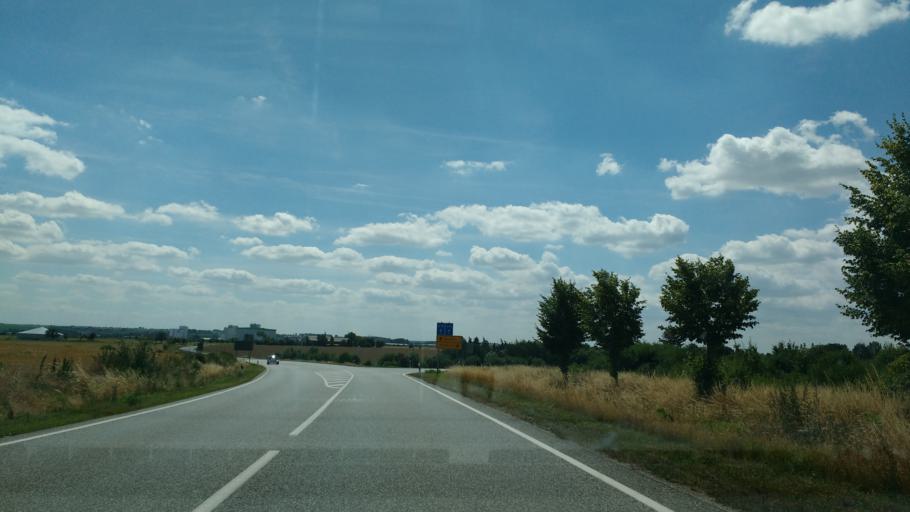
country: DE
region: Saxony-Anhalt
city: Obhausen
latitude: 51.4055
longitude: 11.6317
